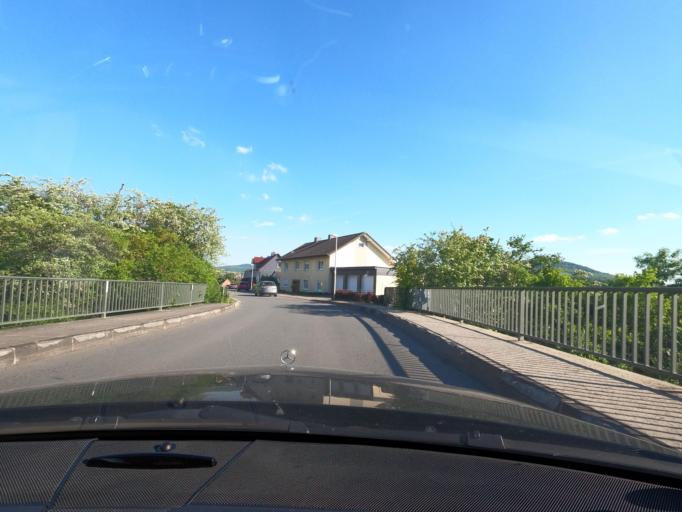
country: DE
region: Hesse
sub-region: Regierungsbezirk Kassel
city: Wolfhagen
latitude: 51.3434
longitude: 9.2291
